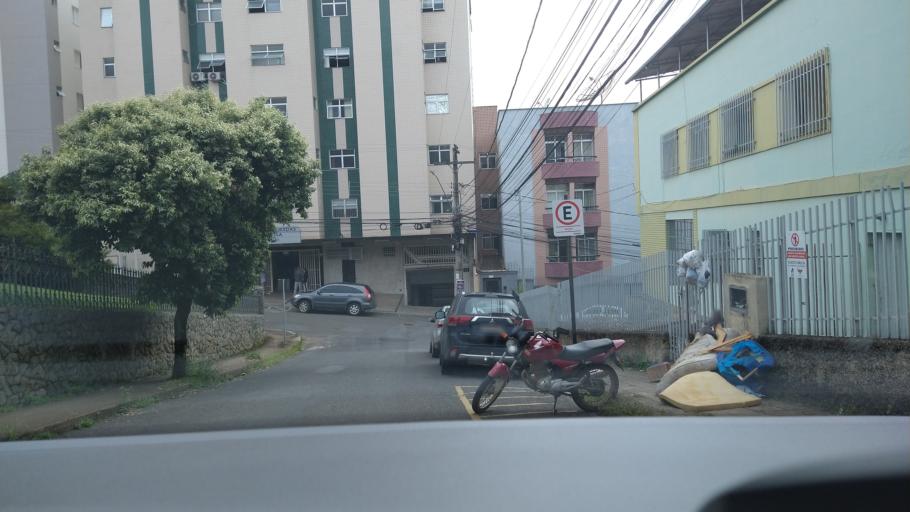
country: BR
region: Minas Gerais
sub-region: Vicosa
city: Vicosa
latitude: -20.7582
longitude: -42.8812
